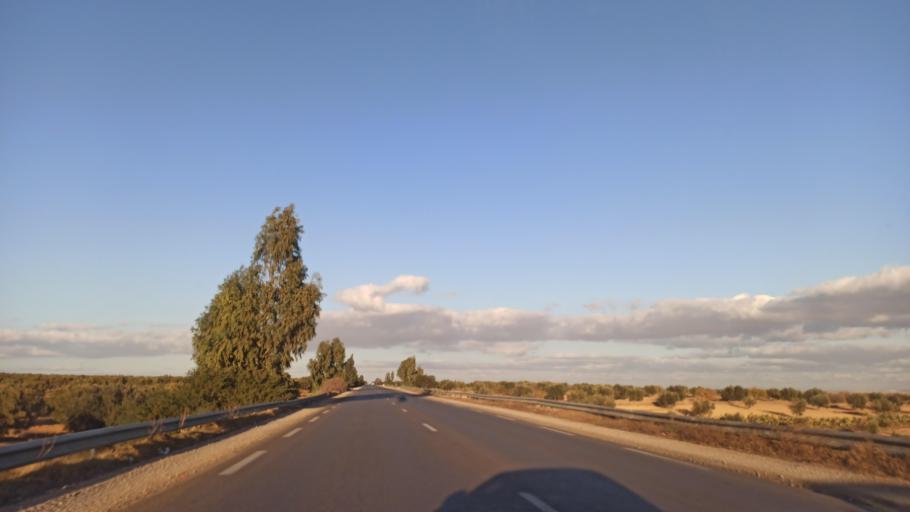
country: TN
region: Al Qayrawan
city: Sbikha
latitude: 35.8593
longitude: 10.2048
